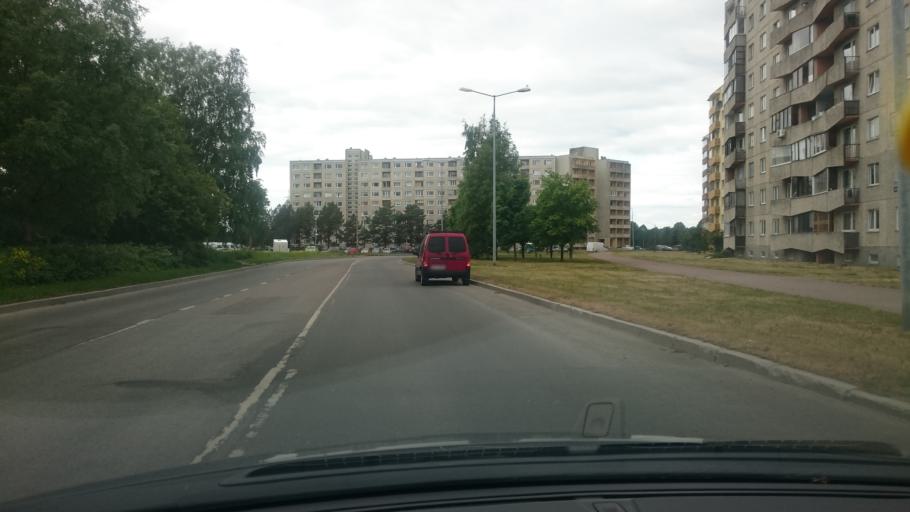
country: EE
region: Harju
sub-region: Saue vald
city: Laagri
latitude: 59.4074
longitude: 24.6355
